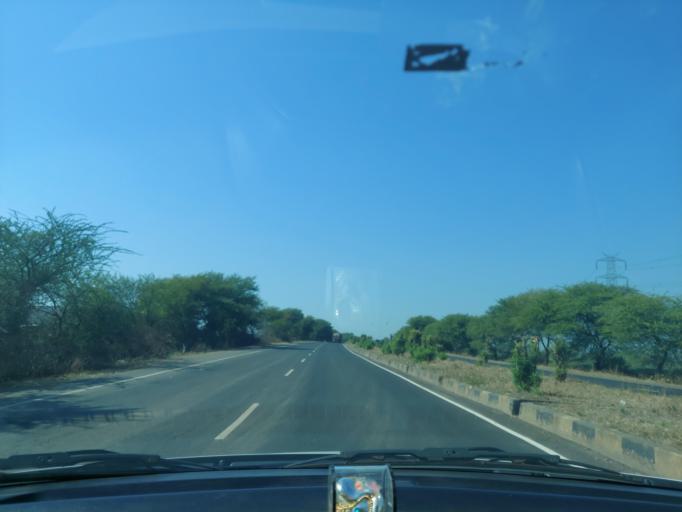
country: IN
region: Madhya Pradesh
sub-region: Indore
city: Manpur
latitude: 22.5022
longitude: 75.5547
